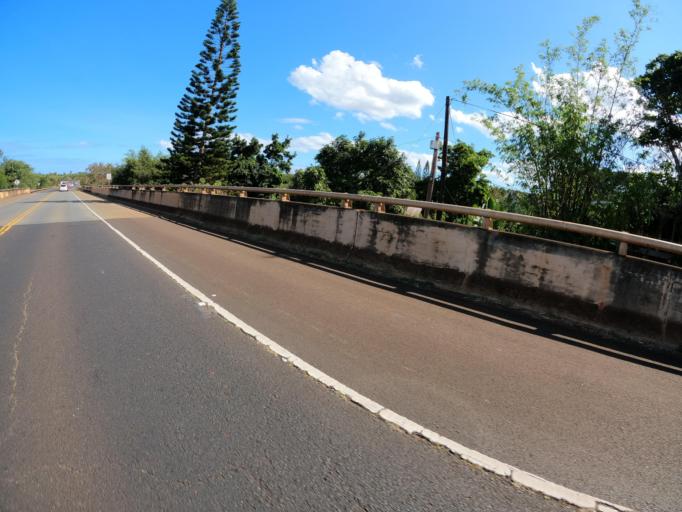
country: US
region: Hawaii
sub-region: Honolulu County
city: Hale'iwa
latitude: 21.5924
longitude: -158.1003
